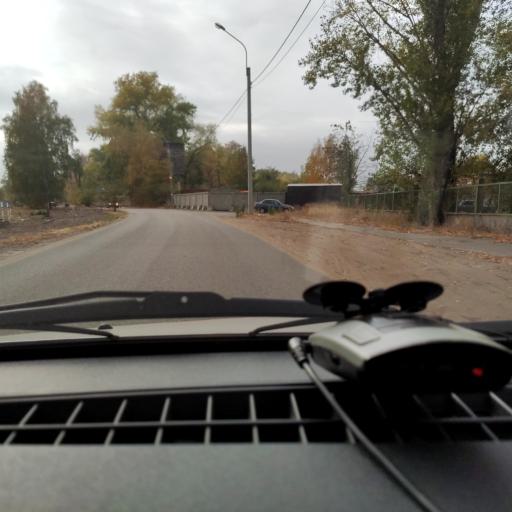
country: RU
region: Voronezj
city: Podgornoye
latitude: 51.7431
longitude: 39.1739
